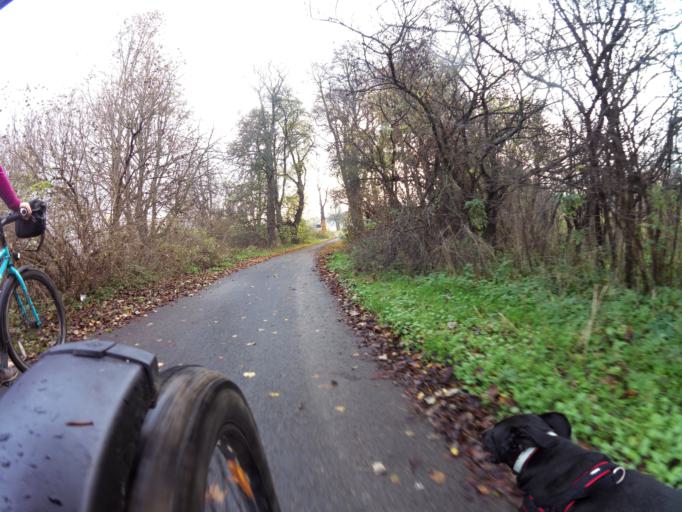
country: PL
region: Pomeranian Voivodeship
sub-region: Powiat wejherowski
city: Gniewino
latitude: 54.7111
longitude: 18.0978
